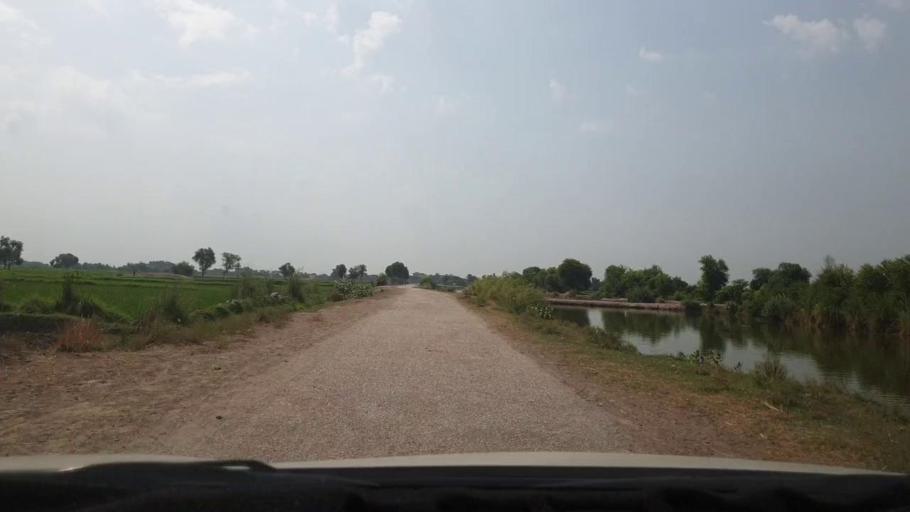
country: PK
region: Sindh
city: Dokri
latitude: 27.3857
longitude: 68.1235
